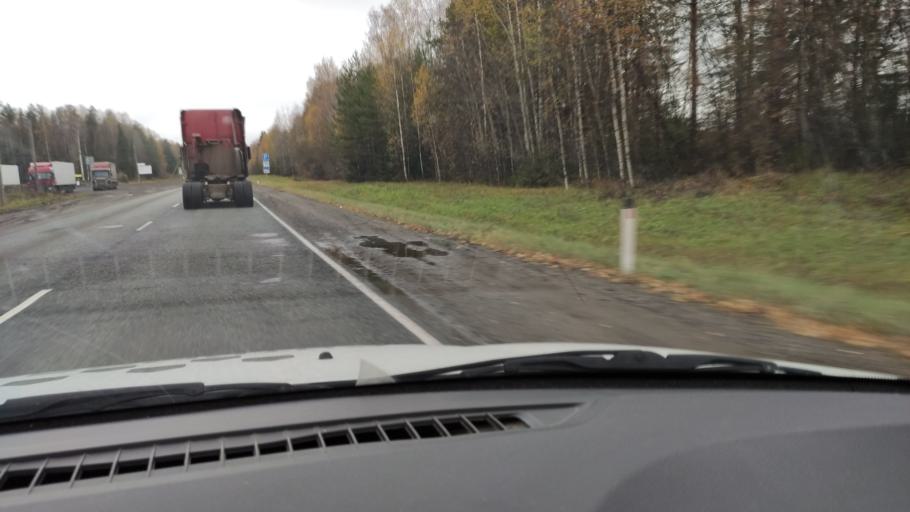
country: RU
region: Kirov
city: Belaya Kholunitsa
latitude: 58.8501
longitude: 50.7222
